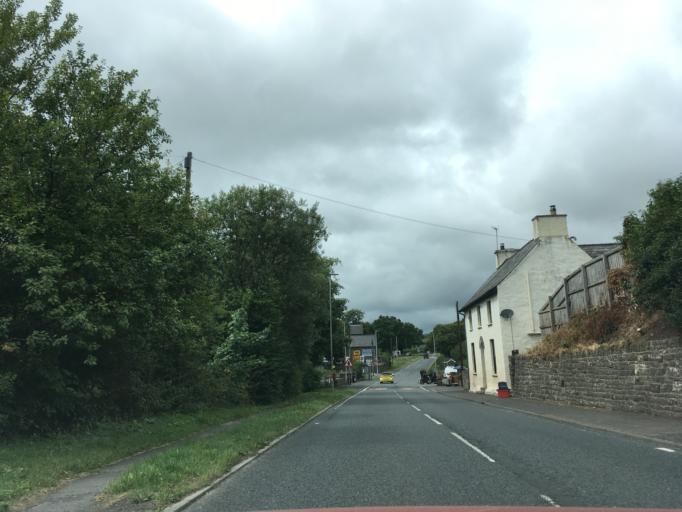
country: GB
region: Wales
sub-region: Sir Powys
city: Cray
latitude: 51.9501
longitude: -3.6310
